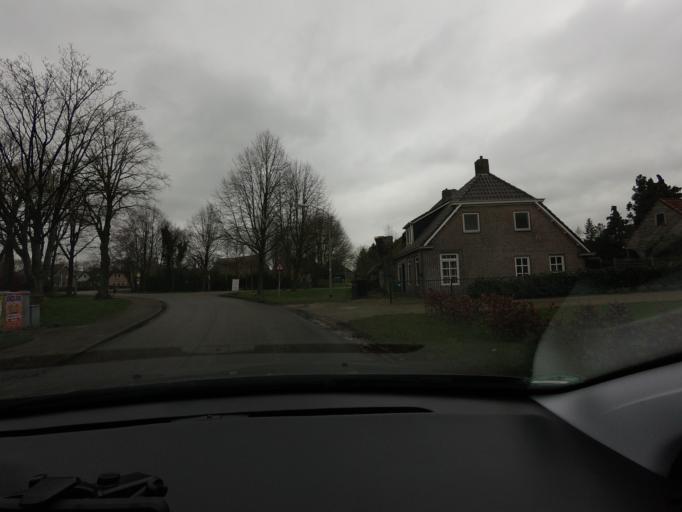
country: NL
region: Drenthe
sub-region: Gemeente Hoogeveen
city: Hoogeveen
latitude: 52.8176
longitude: 6.5167
